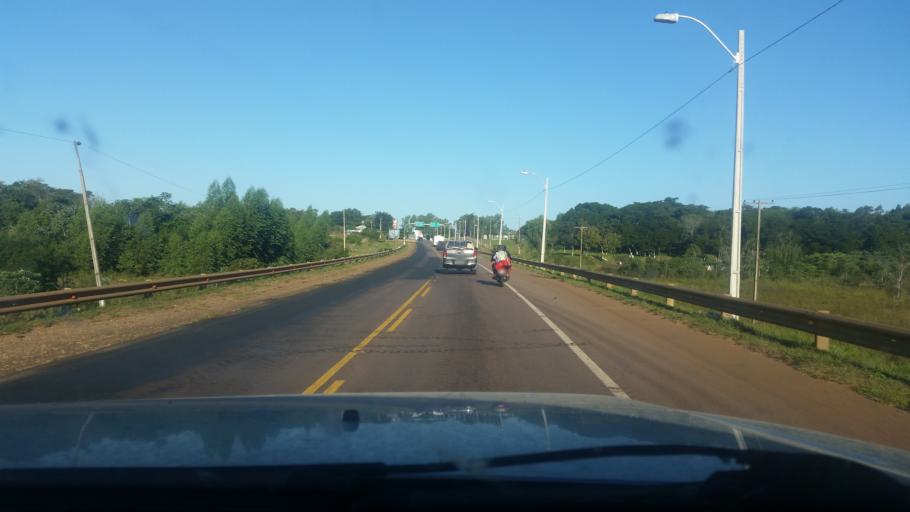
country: PY
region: Guaira
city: Villarrica
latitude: -25.7525
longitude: -56.4406
